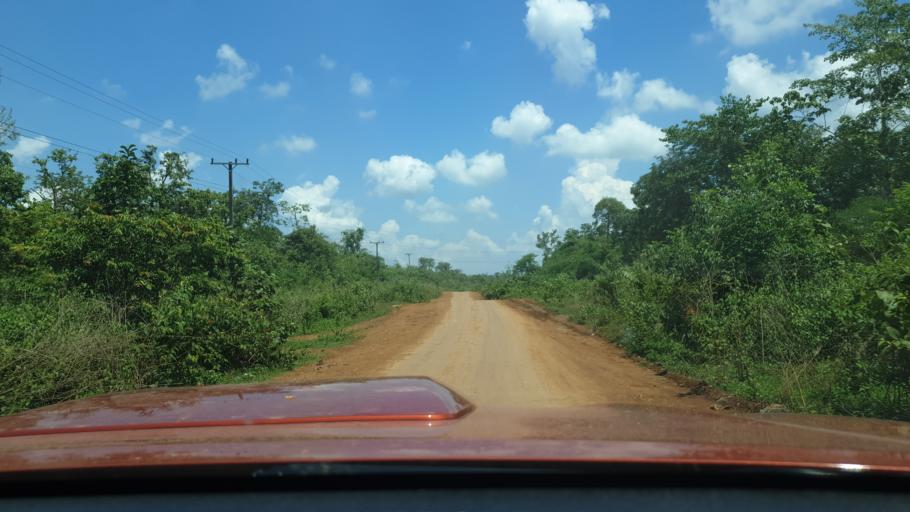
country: LA
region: Champasak
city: Champasak
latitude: 14.7744
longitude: 106.1446
